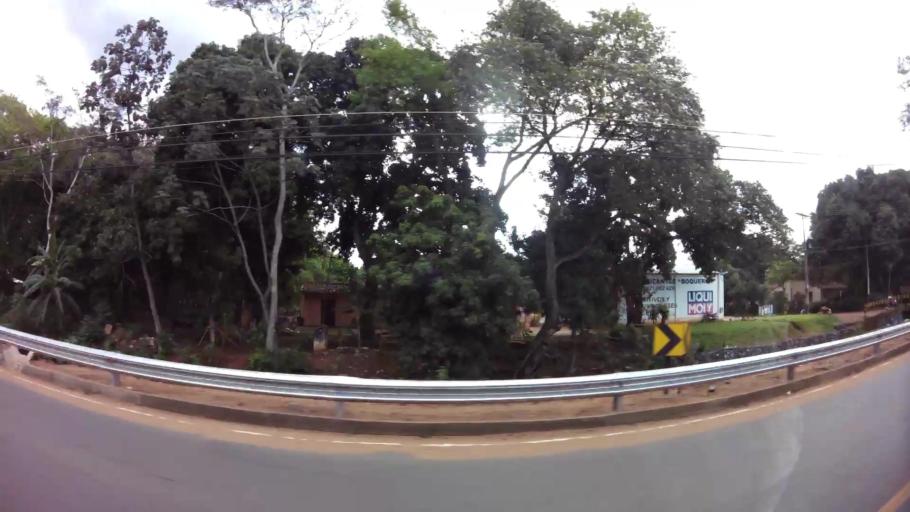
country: PY
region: Central
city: Nemby
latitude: -25.3725
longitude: -57.5439
